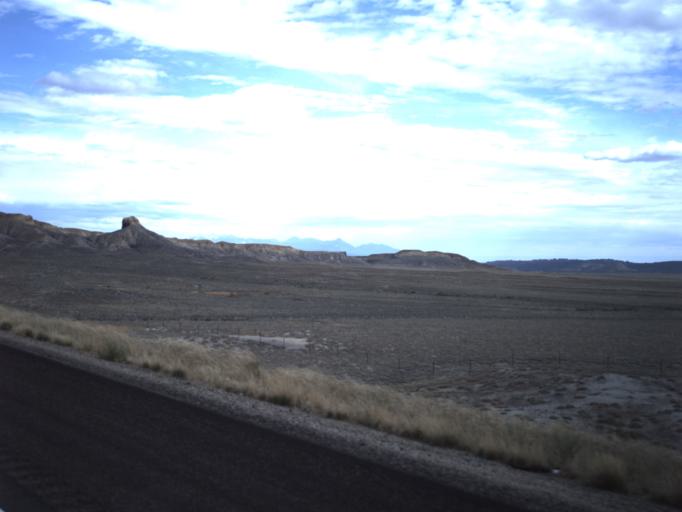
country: US
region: Utah
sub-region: Grand County
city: Moab
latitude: 38.9517
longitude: -109.6966
